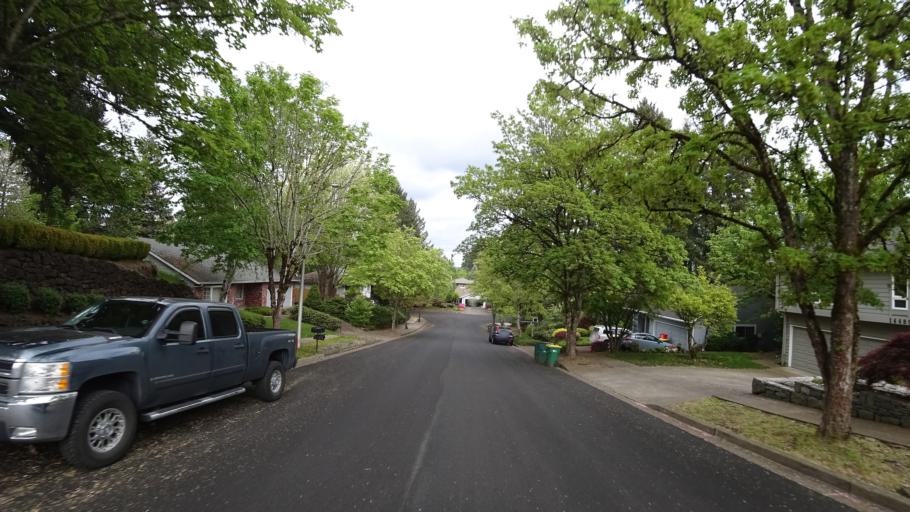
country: US
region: Oregon
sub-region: Washington County
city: Beaverton
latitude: 45.4508
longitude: -122.8242
